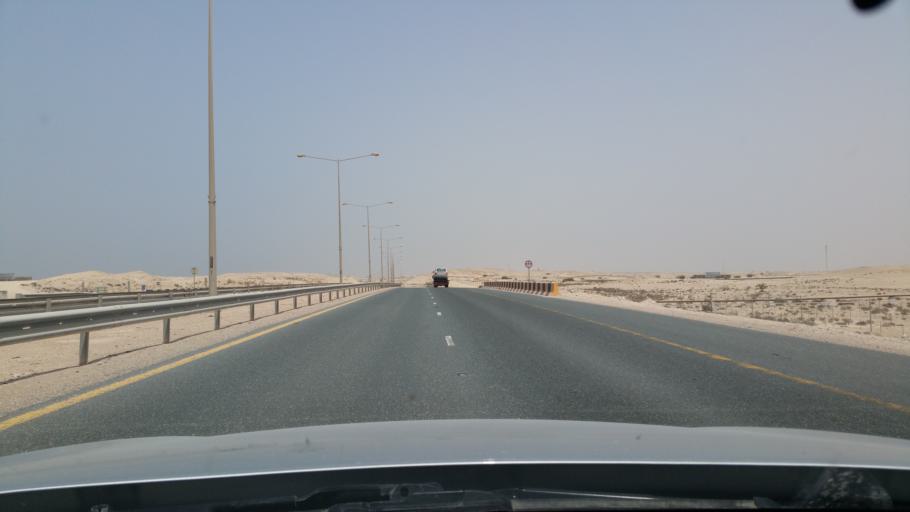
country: QA
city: Umm Bab
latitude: 25.2444
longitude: 50.8004
